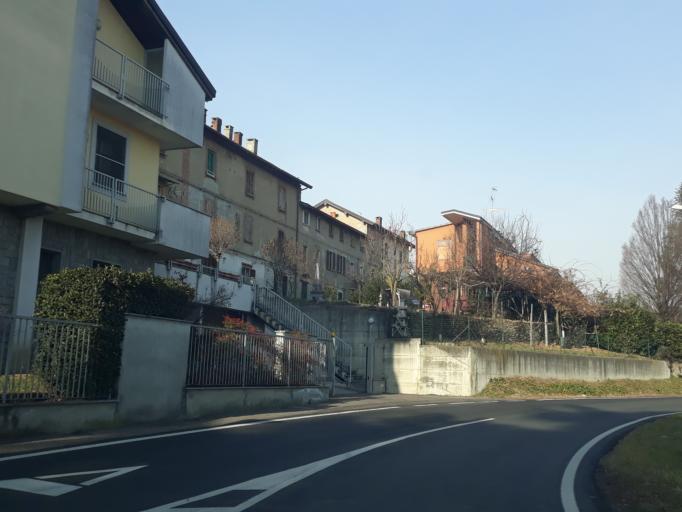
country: IT
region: Lombardy
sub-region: Provincia di Monza e Brianza
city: Bellusco
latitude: 45.6240
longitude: 9.4067
